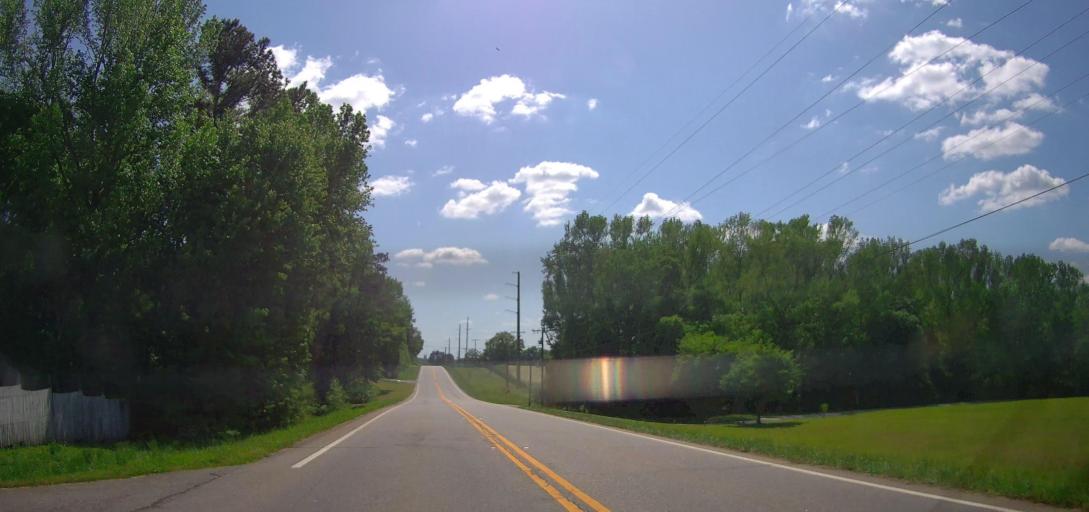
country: US
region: Georgia
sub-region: Putnam County
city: Eatonton
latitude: 33.3404
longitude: -83.3650
